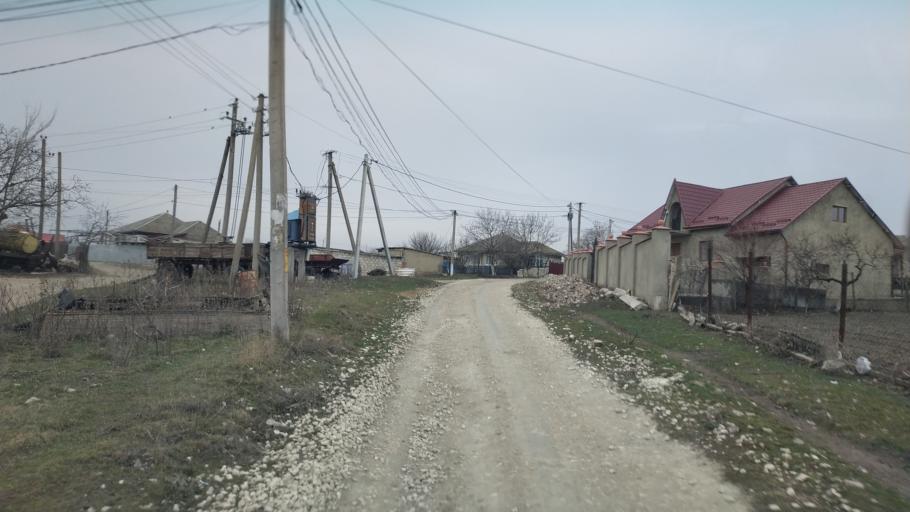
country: MD
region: Chisinau
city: Singera
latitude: 46.8255
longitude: 29.0238
